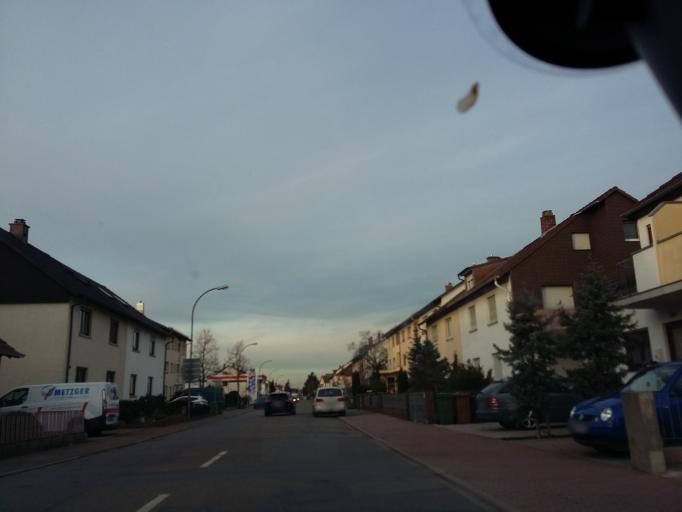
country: DE
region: Baden-Wuerttemberg
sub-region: Karlsruhe Region
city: Hockenheim
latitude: 49.3245
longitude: 8.5465
